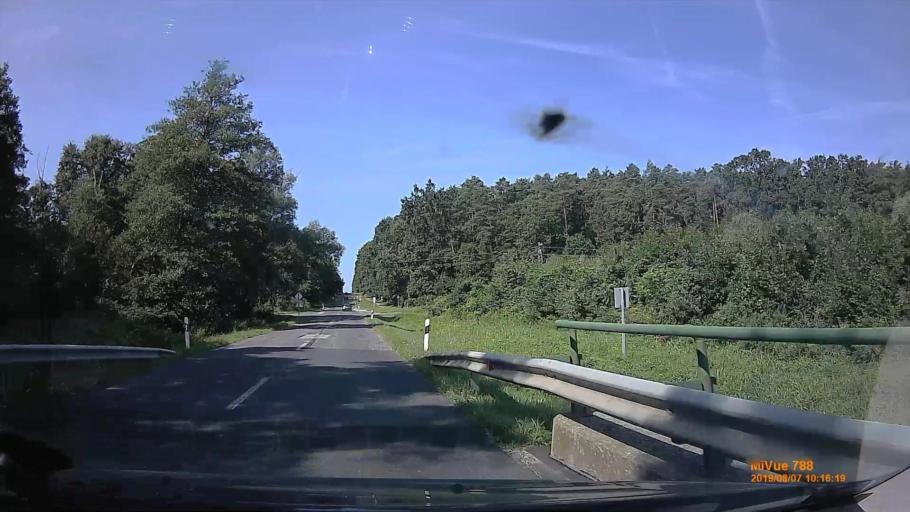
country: HU
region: Zala
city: Lenti
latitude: 46.6403
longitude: 16.5982
